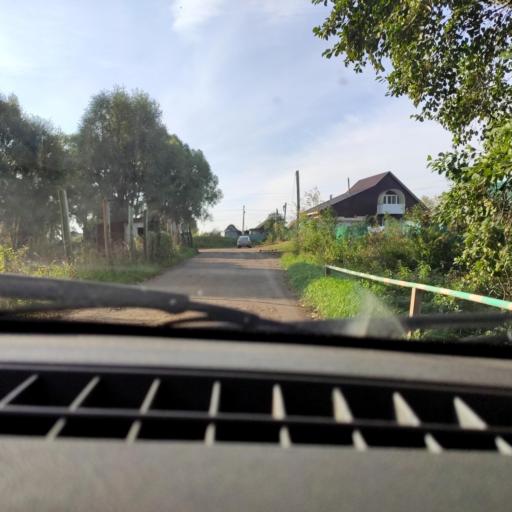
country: RU
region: Bashkortostan
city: Mikhaylovka
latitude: 54.7354
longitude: 55.8303
